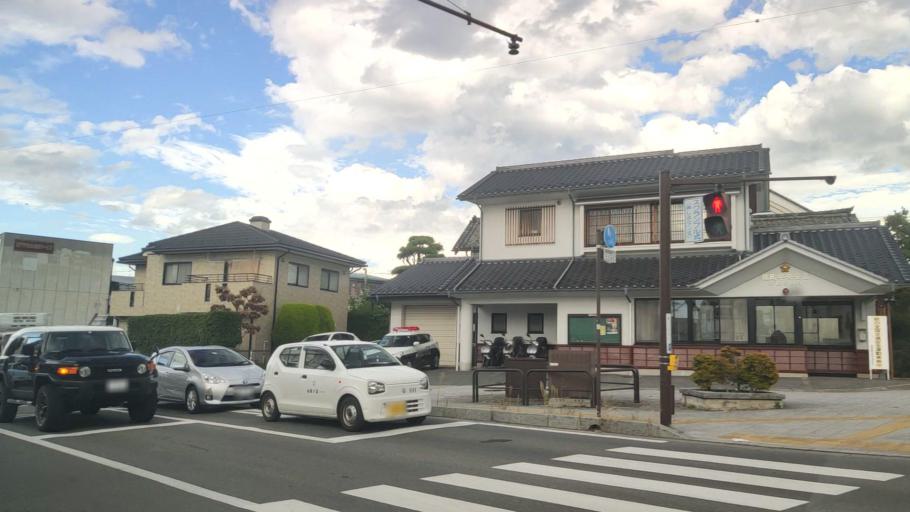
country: JP
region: Nagano
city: Suzaka
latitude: 36.6547
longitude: 138.3074
